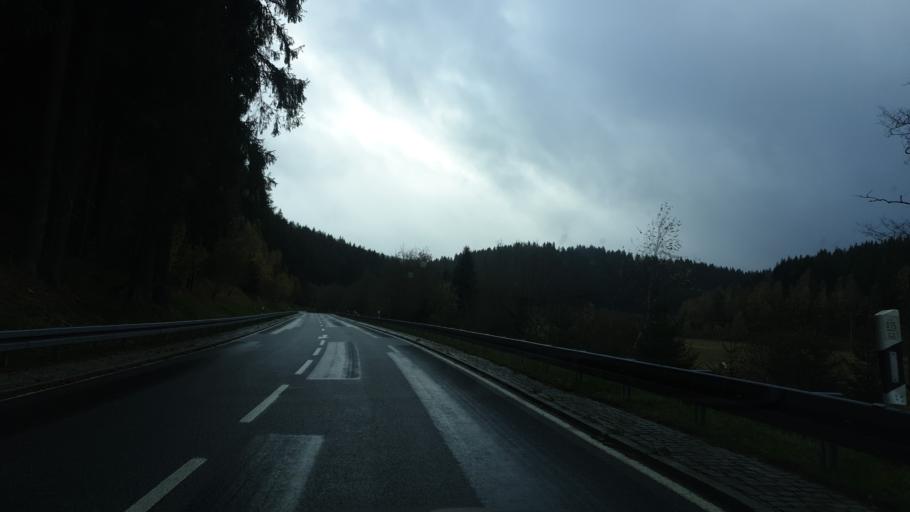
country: DE
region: Saxony
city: Schoenheide
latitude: 50.4883
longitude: 12.5459
